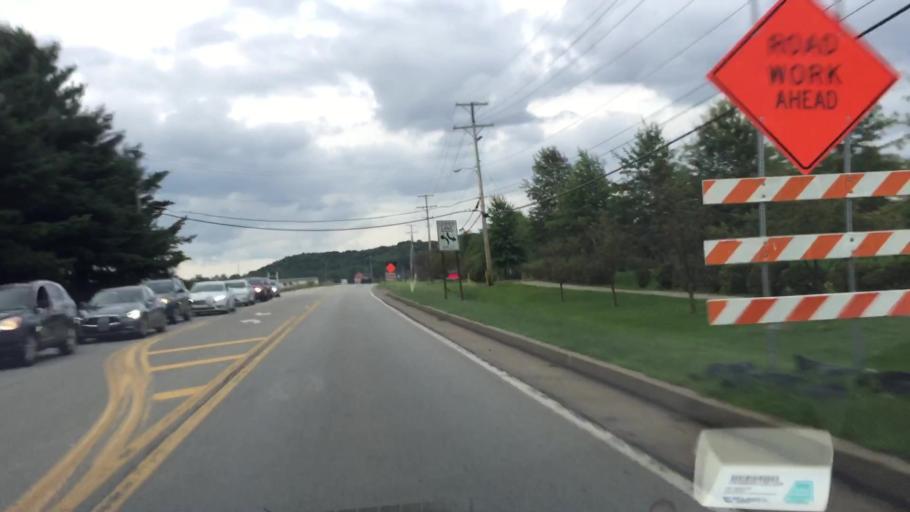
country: US
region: Pennsylvania
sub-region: Butler County
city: Cranberry Township
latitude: 40.6987
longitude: -80.1124
